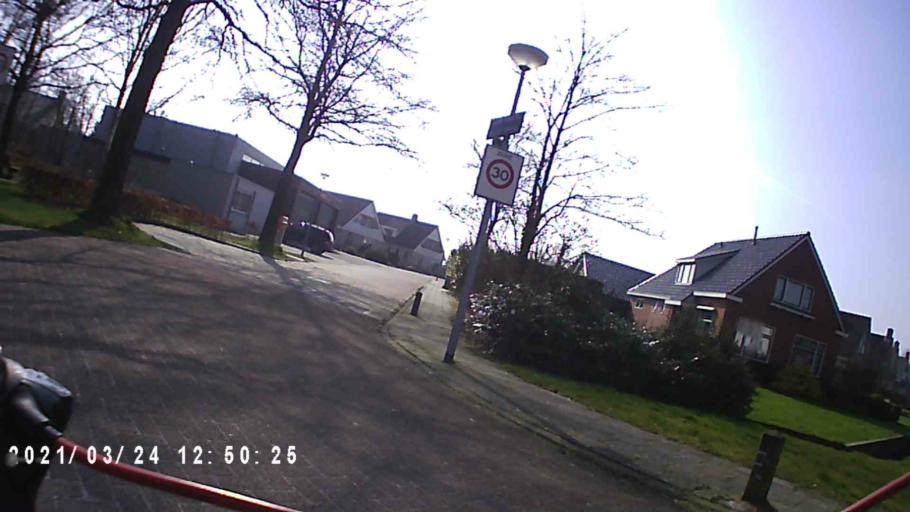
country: NL
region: Groningen
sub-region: Gemeente Leek
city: Leek
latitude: 53.1627
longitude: 6.3291
